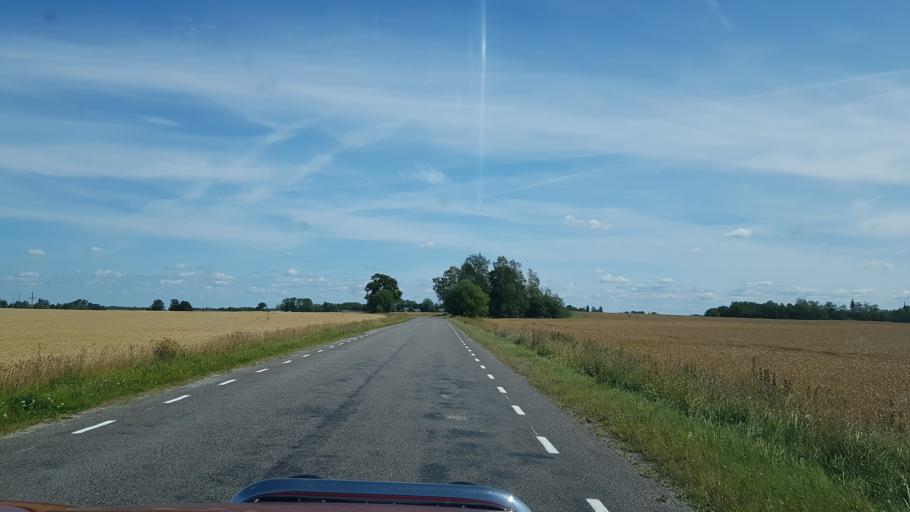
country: EE
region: Jaervamaa
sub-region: Koeru vald
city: Koeru
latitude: 59.0412
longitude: 25.9946
